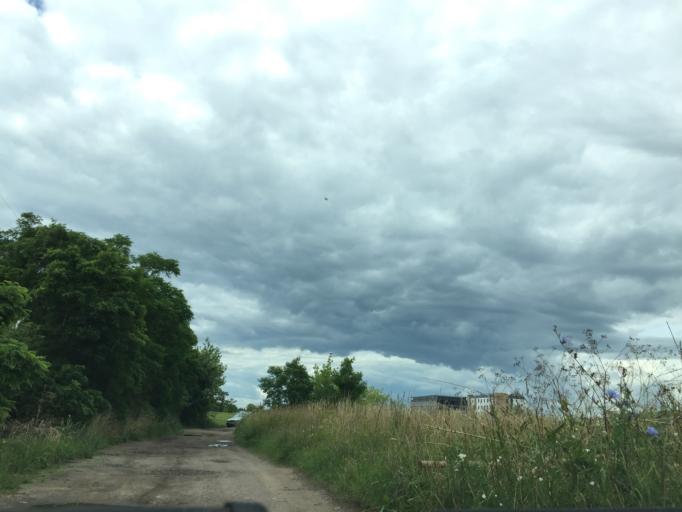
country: PL
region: Podlasie
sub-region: Suwalki
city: Suwalki
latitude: 54.0799
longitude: 22.9383
